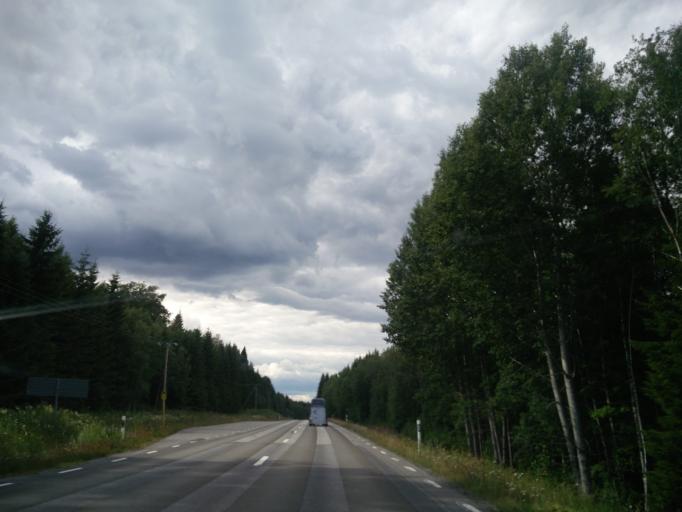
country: SE
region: OErebro
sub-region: Hallefors Kommun
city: Haellefors
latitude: 59.7712
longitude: 14.3987
